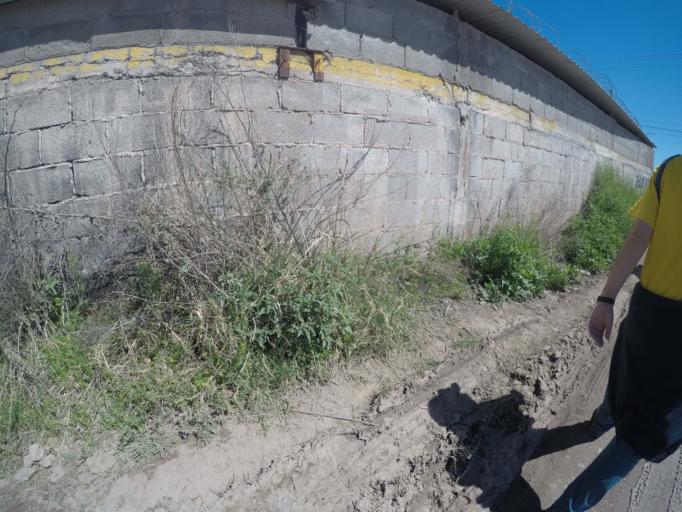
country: US
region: Texas
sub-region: El Paso County
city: Socorro Mission Number 1 Colonia
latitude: 31.6061
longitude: -106.3107
